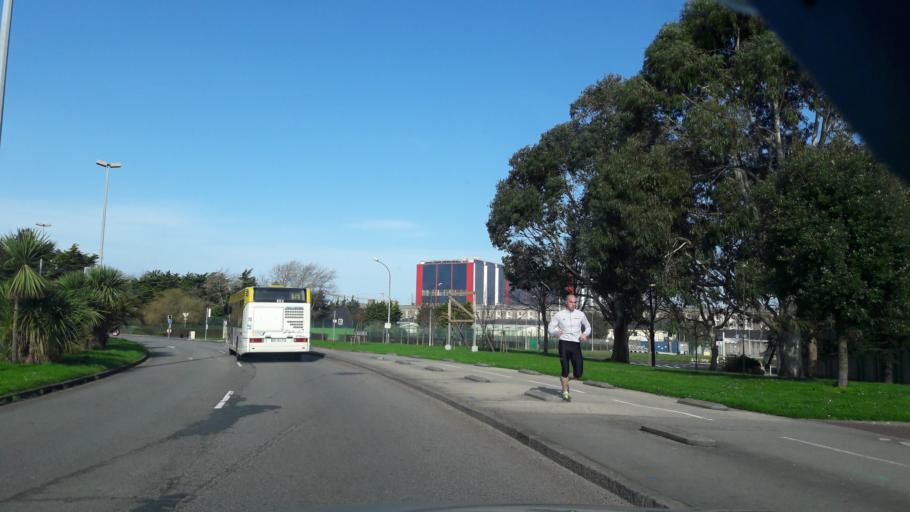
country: FR
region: Lower Normandy
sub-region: Departement de la Manche
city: Cherbourg-Octeville
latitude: 49.6448
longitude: -1.6274
